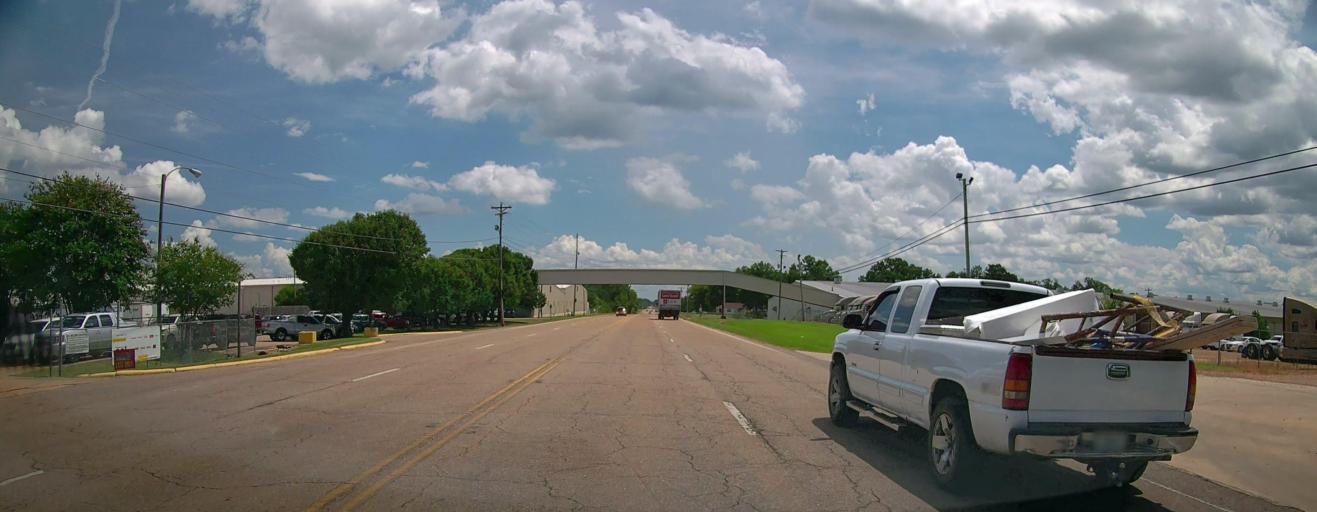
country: US
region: Mississippi
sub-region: Lee County
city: Verona
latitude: 34.1619
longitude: -88.7195
